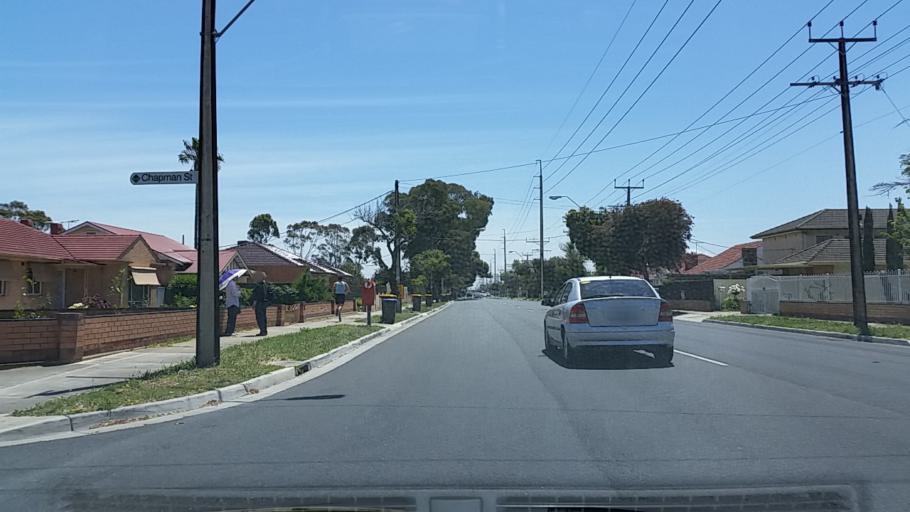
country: AU
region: South Australia
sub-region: Charles Sturt
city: Findon
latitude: -34.8988
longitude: 138.5321
